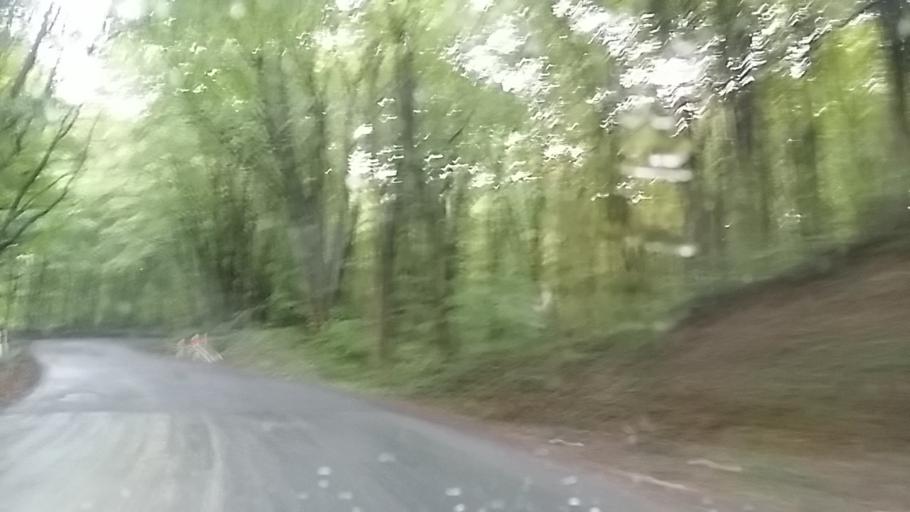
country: HU
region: Komarom-Esztergom
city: Kesztolc
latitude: 47.7360
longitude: 18.8164
